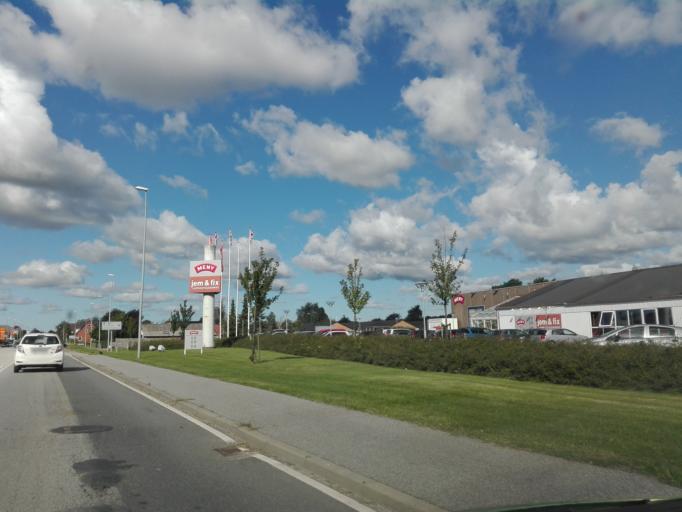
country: DK
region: North Denmark
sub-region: Mariagerfjord Kommune
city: Hobro
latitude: 56.6264
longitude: 9.8041
